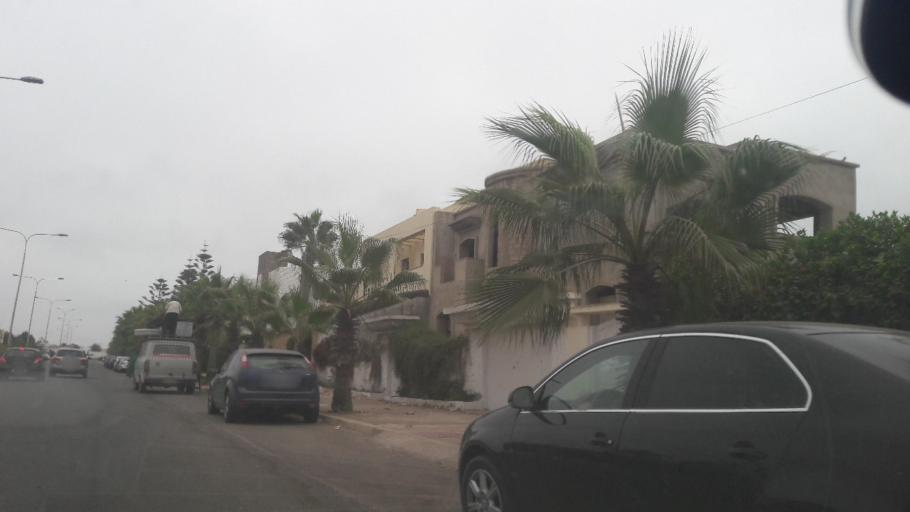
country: MA
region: Souss-Massa-Draa
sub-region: Agadir-Ida-ou-Tnan
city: Agadir
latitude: 30.3922
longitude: -9.5950
